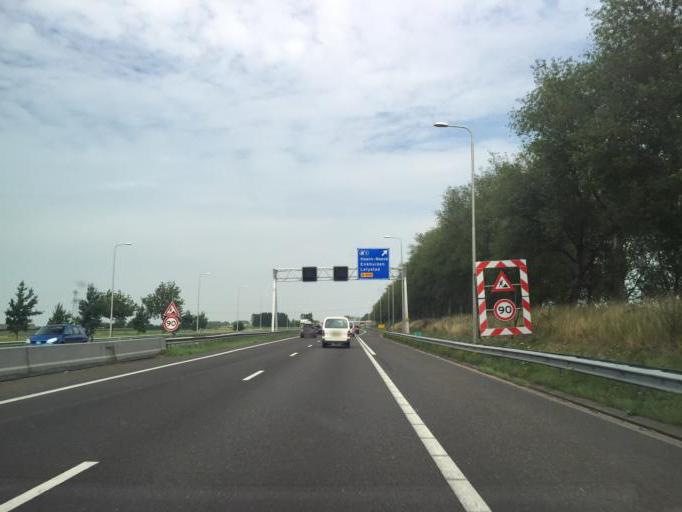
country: NL
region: North Holland
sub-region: Gemeente Hoorn
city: Hoorn
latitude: 52.6627
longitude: 5.0361
